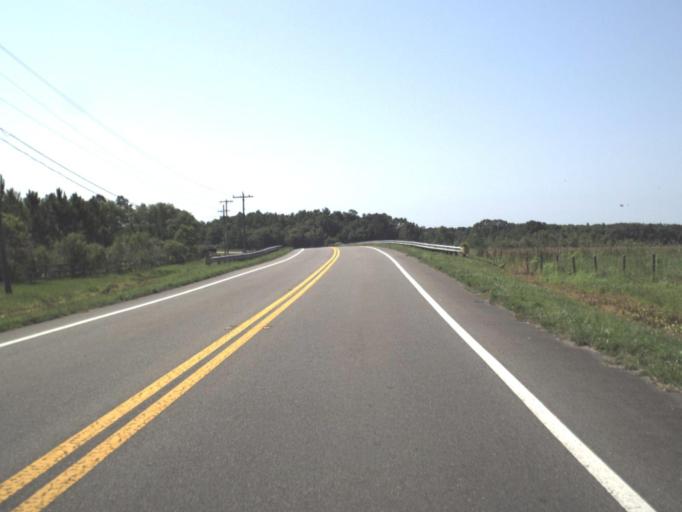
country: US
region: Florida
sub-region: Nassau County
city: Nassau Village-Ratliff
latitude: 30.5130
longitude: -81.7592
